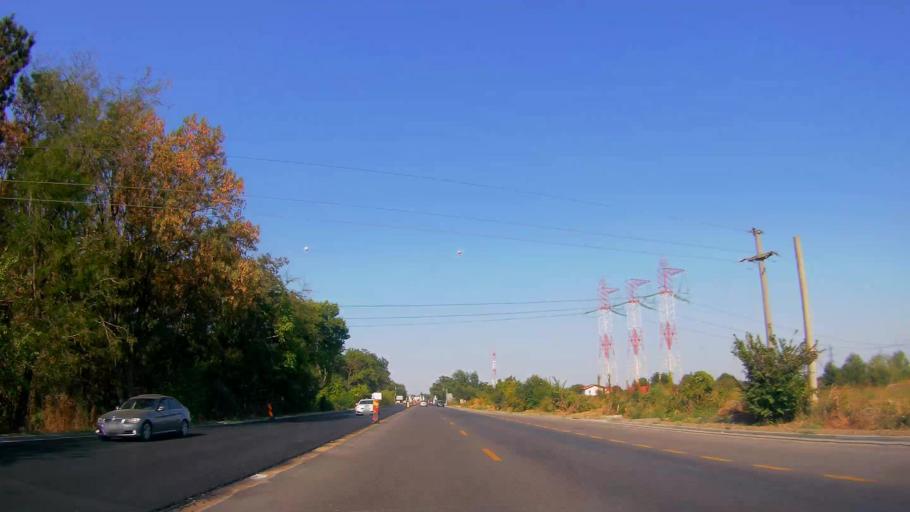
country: RO
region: Ilfov
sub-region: Comuna Jilava
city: Jilava
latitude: 44.3197
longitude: 26.0692
